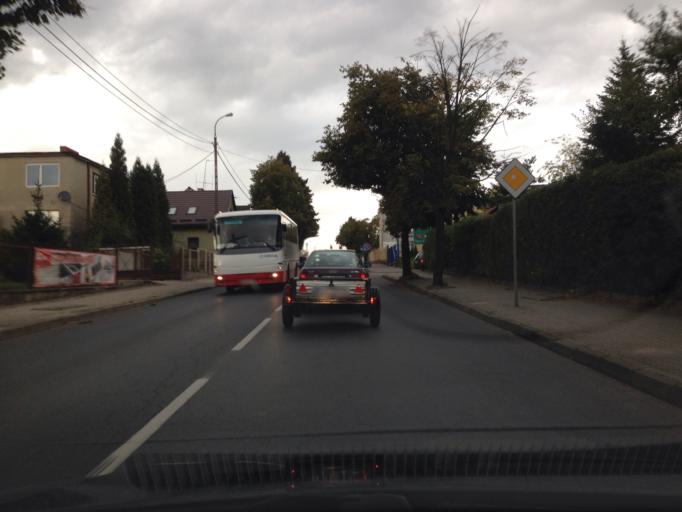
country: PL
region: Kujawsko-Pomorskie
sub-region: Powiat lipnowski
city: Lipno
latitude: 52.8507
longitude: 19.1755
